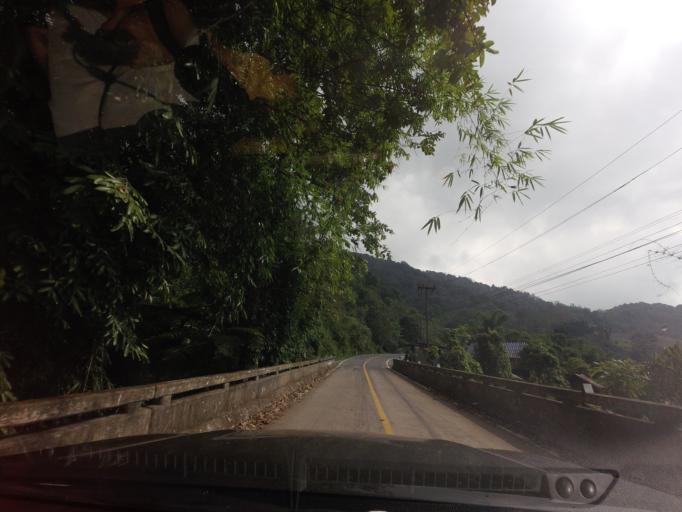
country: TH
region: Nan
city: Bo Kluea
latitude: 19.1885
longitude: 101.0781
